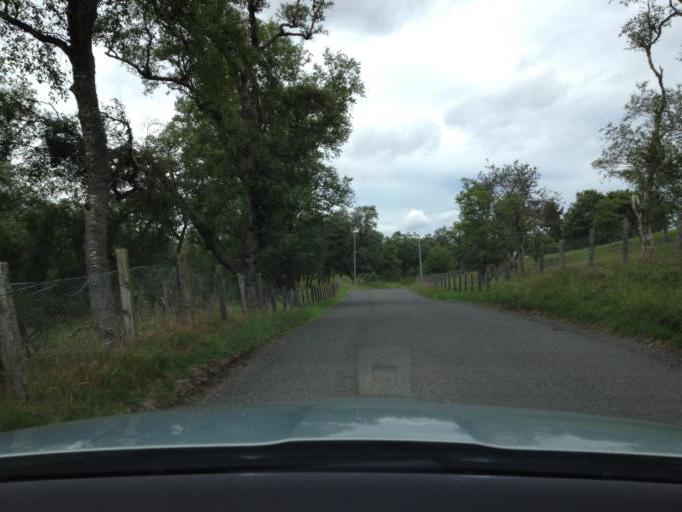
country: GB
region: Scotland
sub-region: Aberdeenshire
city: Aboyne
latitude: 56.9007
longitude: -2.8222
